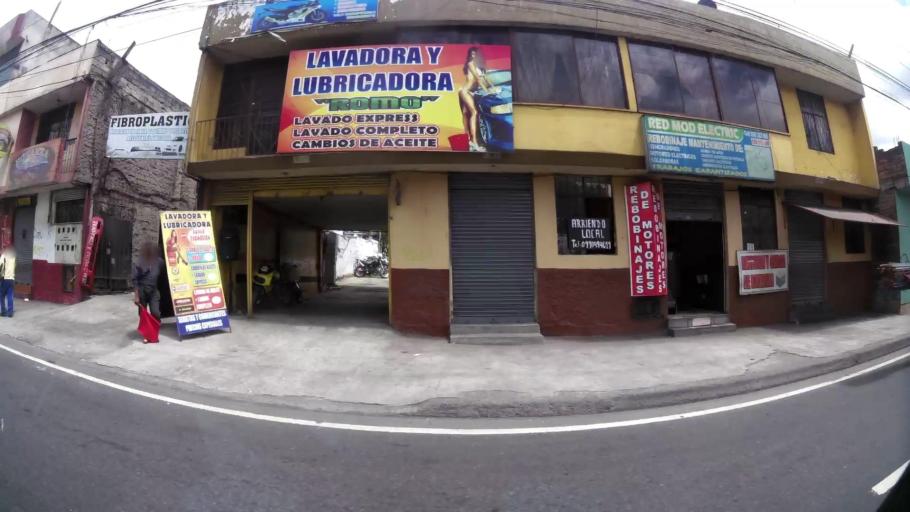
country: EC
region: Pichincha
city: Sangolqui
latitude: -0.3358
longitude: -78.5502
